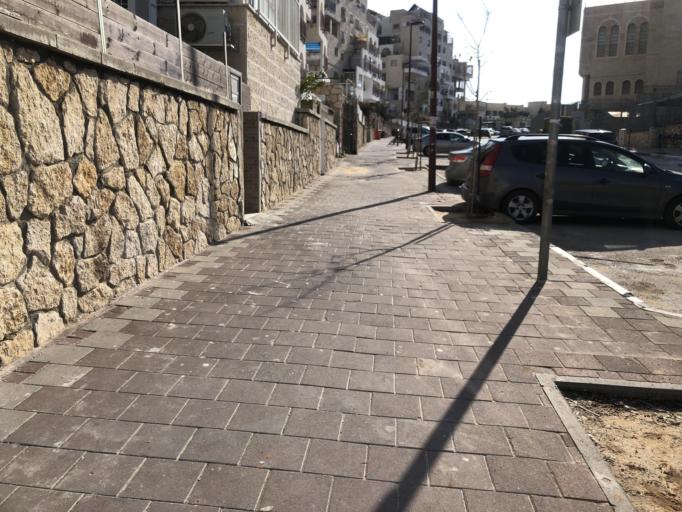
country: PS
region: West Bank
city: Dayr Qiddis
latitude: 31.9411
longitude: 35.0454
